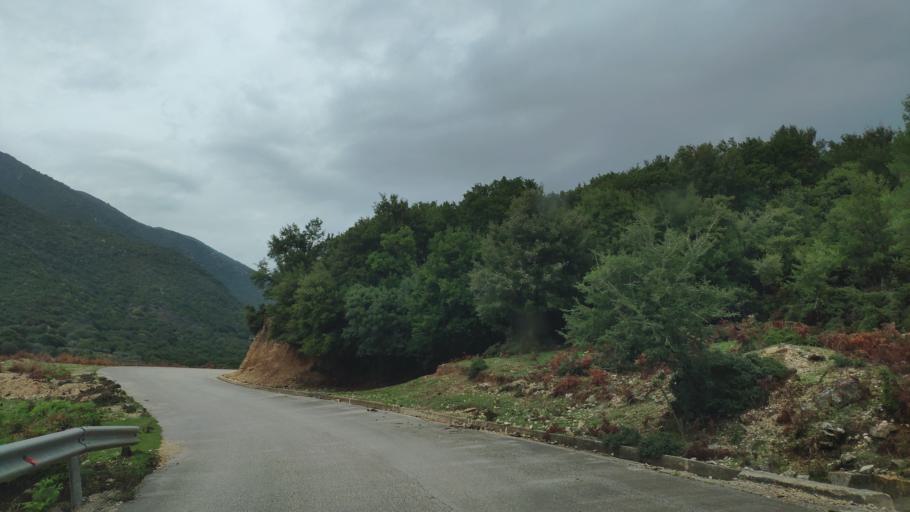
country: GR
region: Epirus
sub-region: Nomos Thesprotias
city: Paramythia
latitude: 39.3870
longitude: 20.6240
